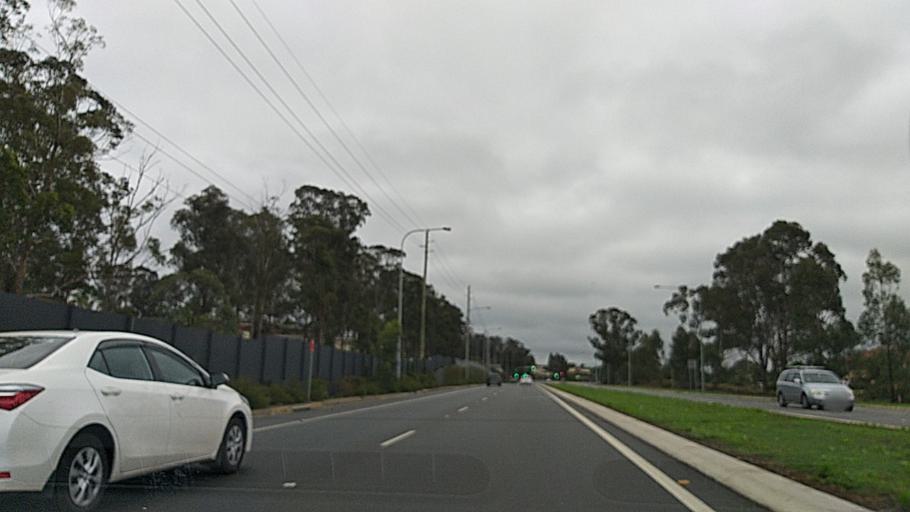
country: AU
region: New South Wales
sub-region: Penrith Municipality
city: Werrington Downs
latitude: -33.7248
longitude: 150.7214
